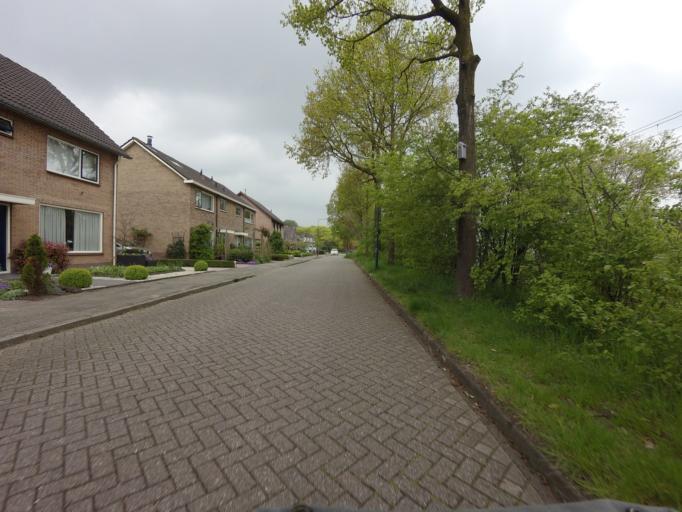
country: NL
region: Utrecht
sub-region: Gemeente IJsselstein
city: IJsselstein
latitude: 52.0255
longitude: 5.0505
